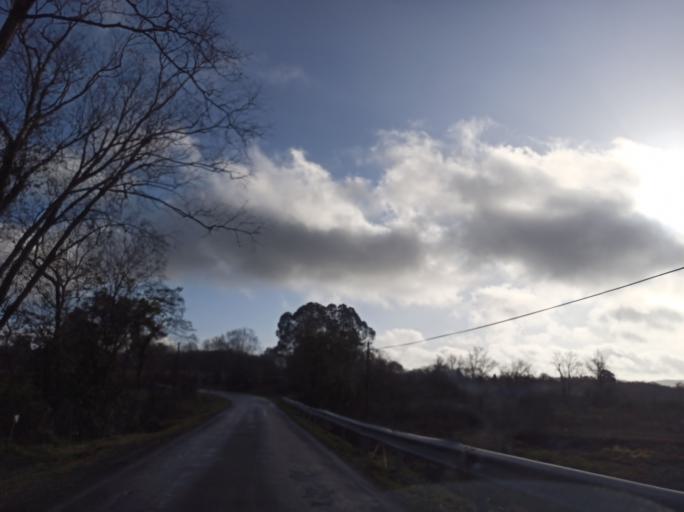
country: ES
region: Galicia
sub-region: Provincia da Coruna
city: Curtis
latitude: 43.0968
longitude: -7.9886
